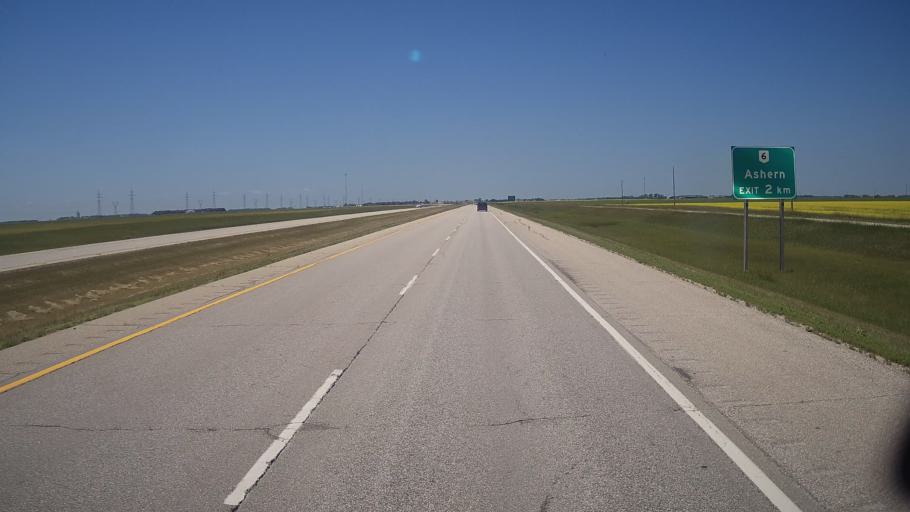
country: CA
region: Manitoba
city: Stonewall
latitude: 49.9900
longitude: -97.2830
